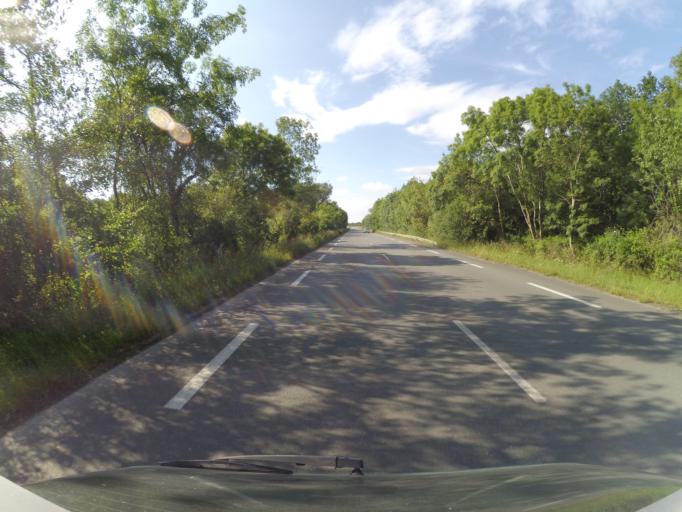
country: FR
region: Poitou-Charentes
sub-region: Departement de la Charente-Maritime
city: Saint-Agnant
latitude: 45.8278
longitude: -0.9355
